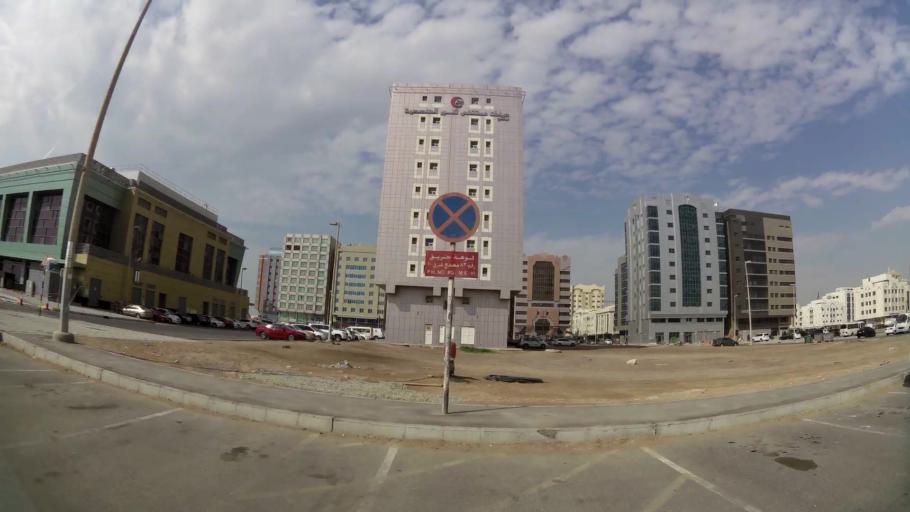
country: AE
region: Abu Dhabi
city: Abu Dhabi
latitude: 24.3322
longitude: 54.5315
